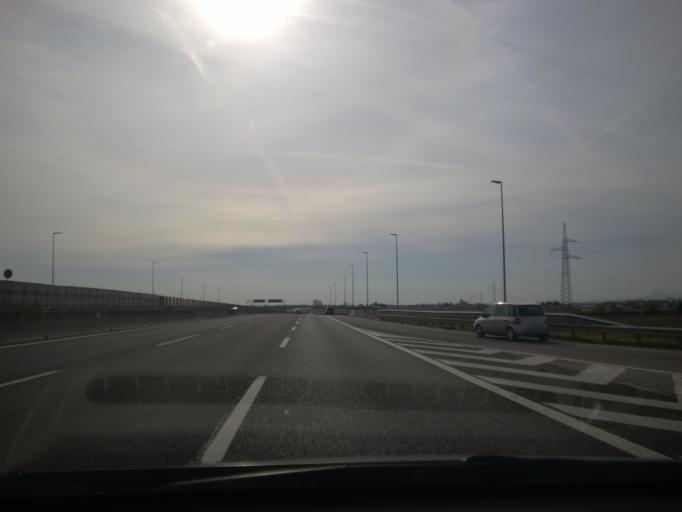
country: IT
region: Emilia-Romagna
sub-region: Forli-Cesena
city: Cesena
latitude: 44.1681
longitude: 12.2879
